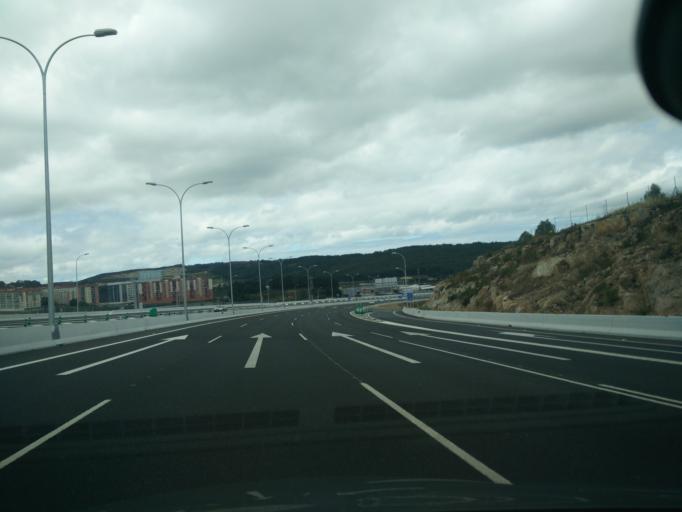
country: ES
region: Galicia
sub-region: Provincia da Coruna
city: Culleredo
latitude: 43.3250
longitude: -8.4195
